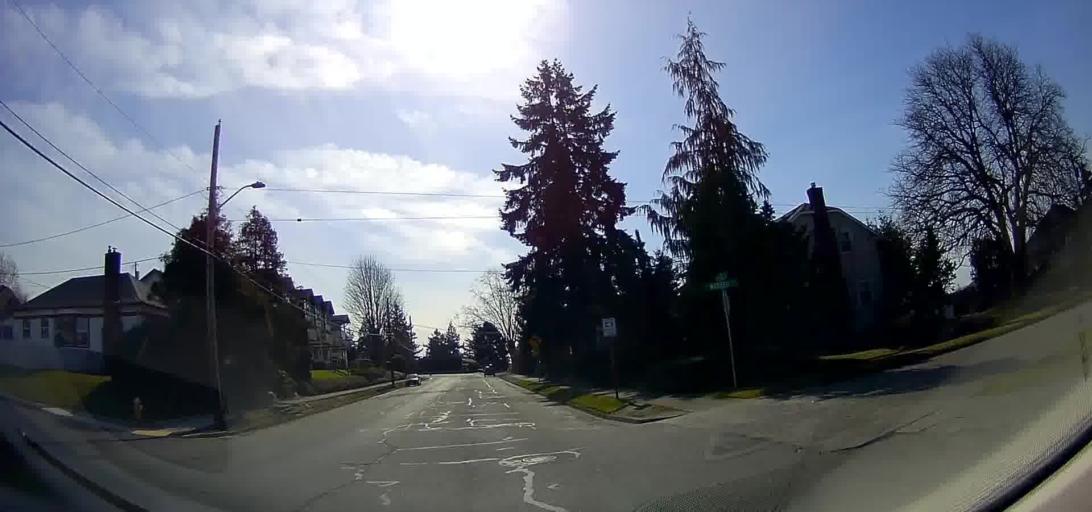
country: US
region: Washington
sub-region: Skagit County
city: Mount Vernon
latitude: 48.4224
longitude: -122.3330
